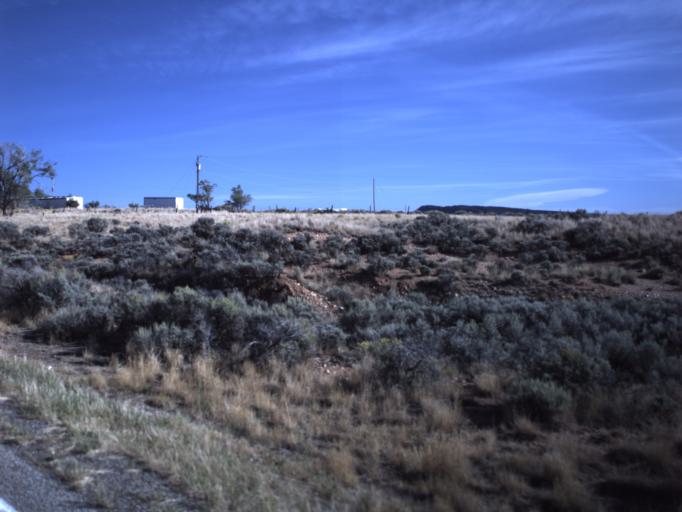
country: US
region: Utah
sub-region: Grand County
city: Moab
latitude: 38.3146
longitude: -109.3064
